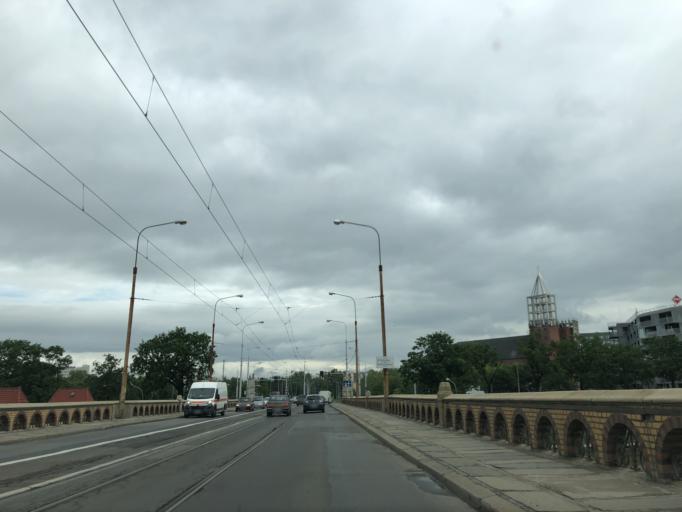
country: PL
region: Lower Silesian Voivodeship
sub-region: Powiat wroclawski
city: Wroclaw
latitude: 51.1318
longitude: 17.0279
